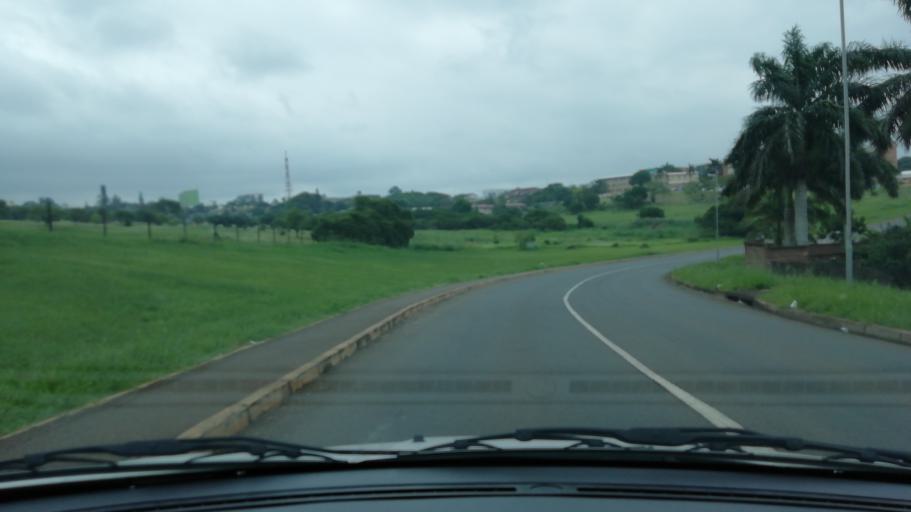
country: ZA
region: KwaZulu-Natal
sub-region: uThungulu District Municipality
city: Empangeni
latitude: -28.7413
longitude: 31.9005
